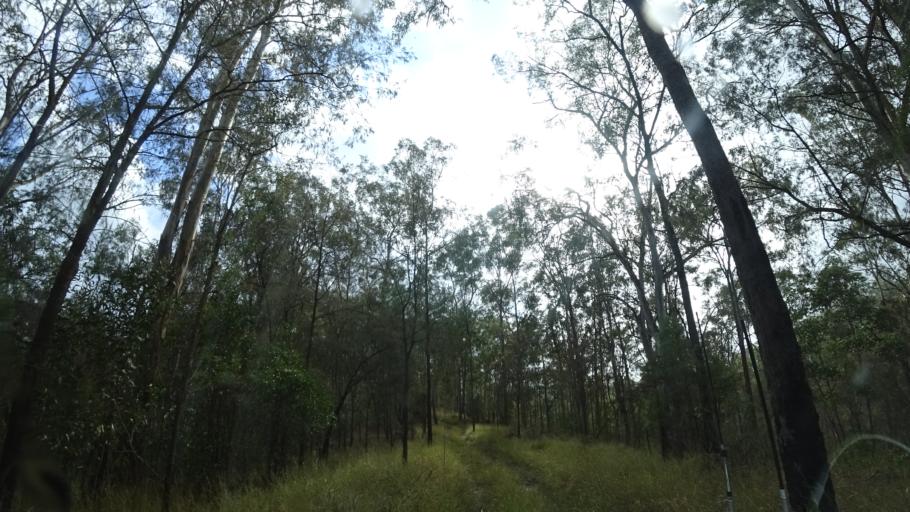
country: AU
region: Queensland
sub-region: Brisbane
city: Pullenvale
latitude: -27.4592
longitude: 152.8684
